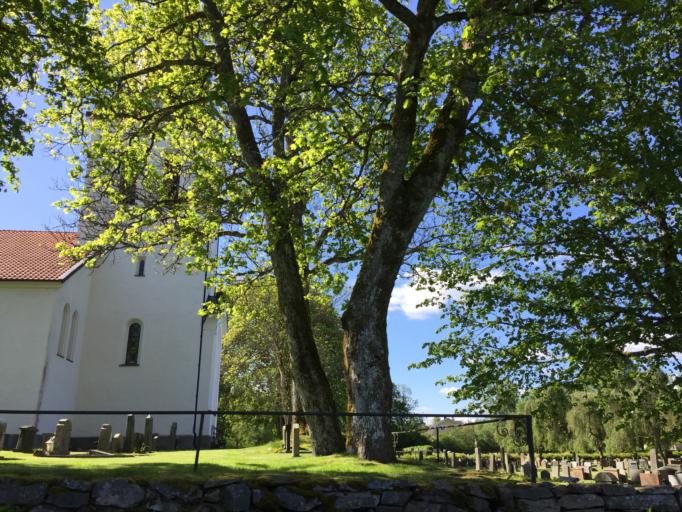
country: SE
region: Kronoberg
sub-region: Markaryds Kommun
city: Stromsnasbruk
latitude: 56.6183
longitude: 13.6084
